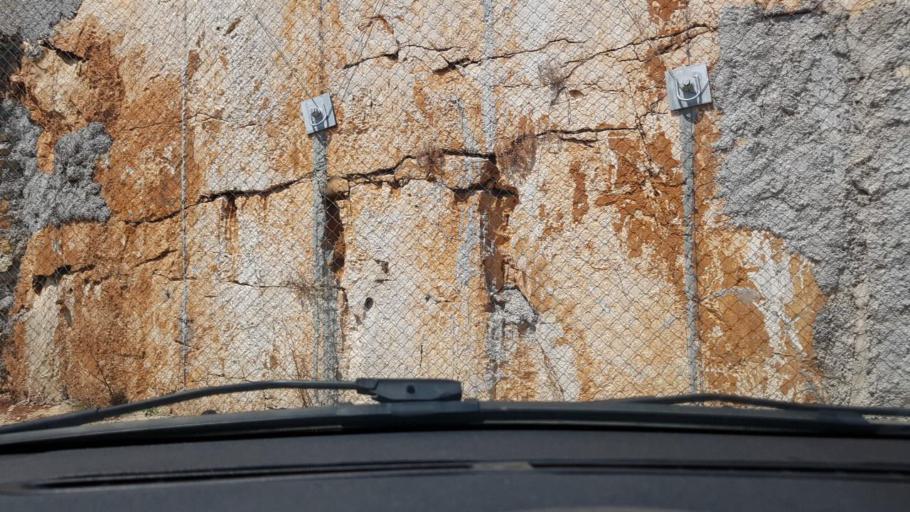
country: HR
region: Splitsko-Dalmatinska
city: Vrgorac
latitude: 43.2052
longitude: 17.3632
